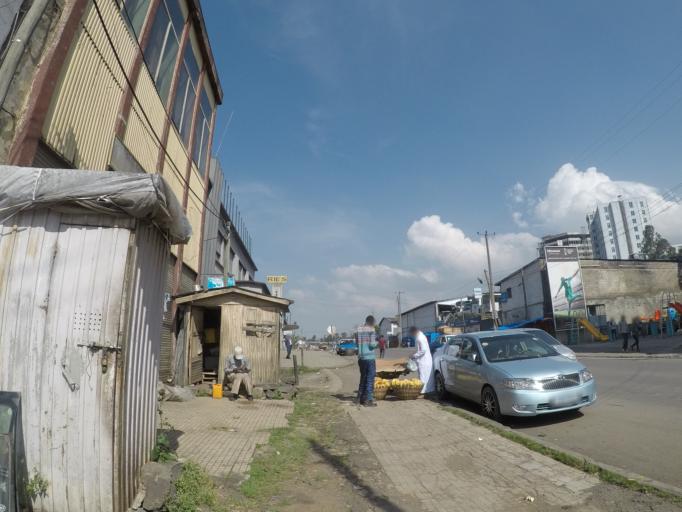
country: ET
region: Adis Abeba
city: Addis Ababa
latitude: 9.0324
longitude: 38.7467
